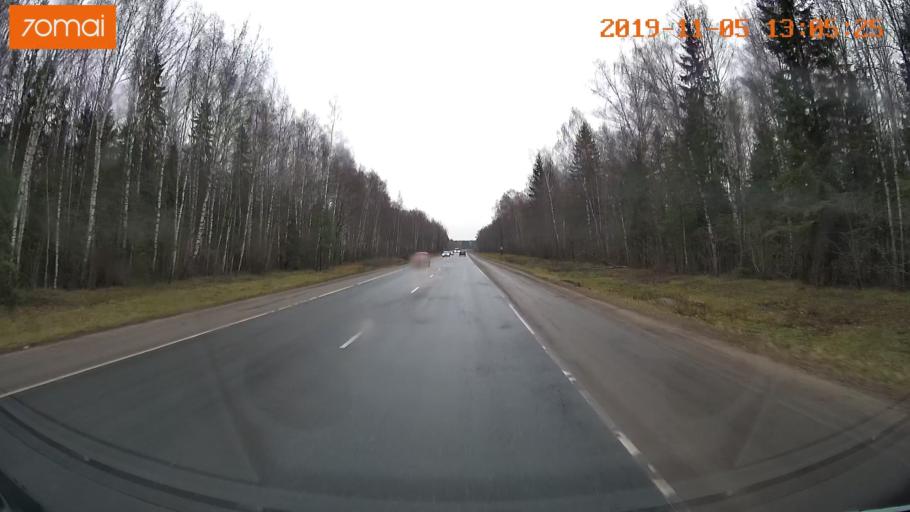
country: RU
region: Ivanovo
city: Kitovo
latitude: 56.8827
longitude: 41.2423
